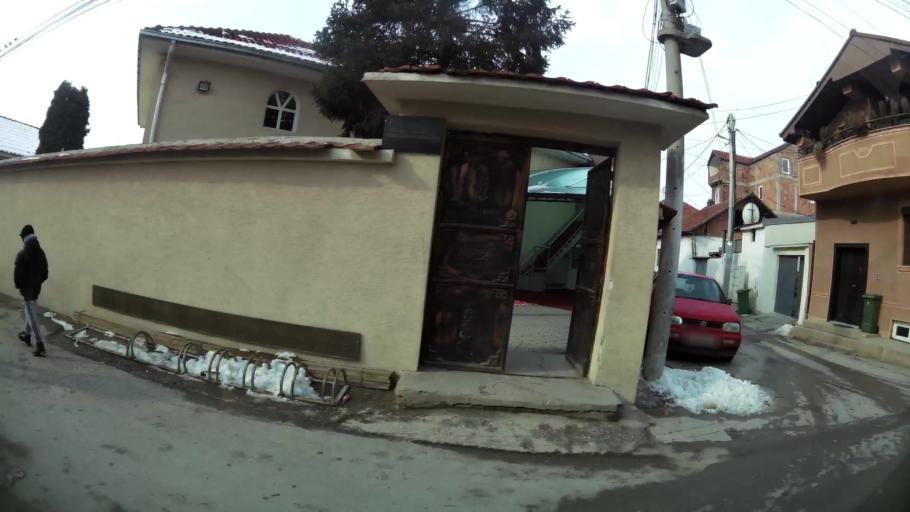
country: MK
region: Cair
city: Cair
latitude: 42.0101
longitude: 21.4377
